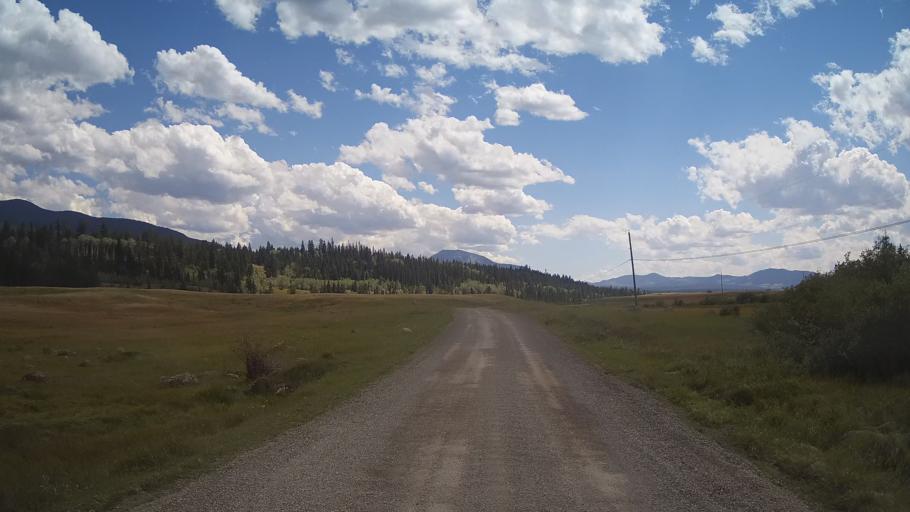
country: CA
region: British Columbia
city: Lillooet
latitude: 51.3225
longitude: -121.9799
